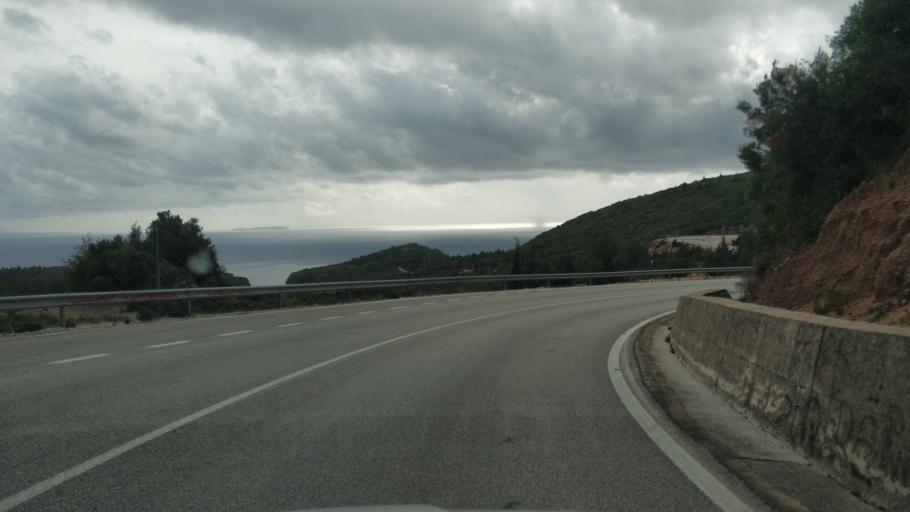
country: AL
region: Vlore
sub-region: Rrethi i Vlores
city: Vranisht
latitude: 40.1420
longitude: 19.6784
